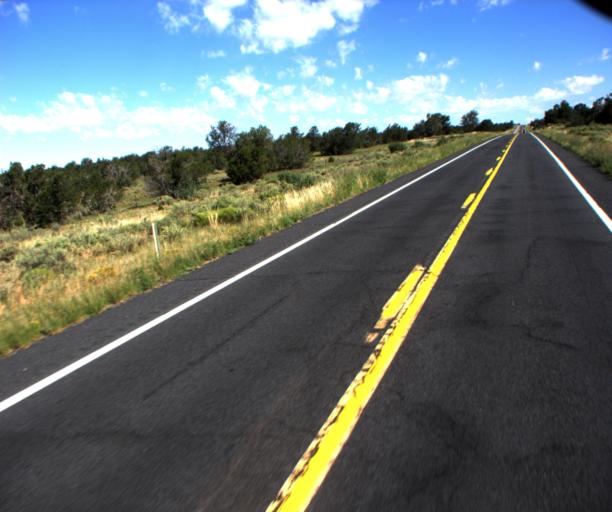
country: US
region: Arizona
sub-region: Coconino County
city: Grand Canyon Village
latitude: 35.8082
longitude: -112.1313
